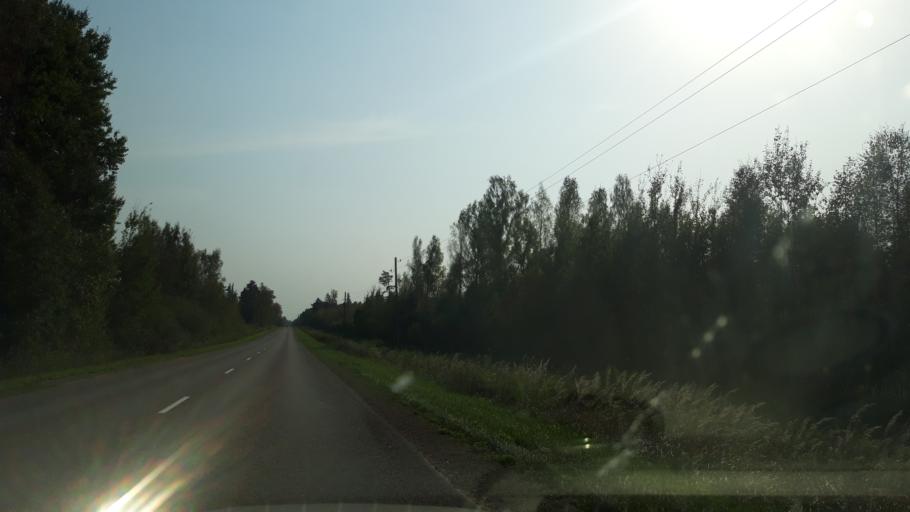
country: LV
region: Burtnieki
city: Matisi
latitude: 57.6485
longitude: 25.2394
